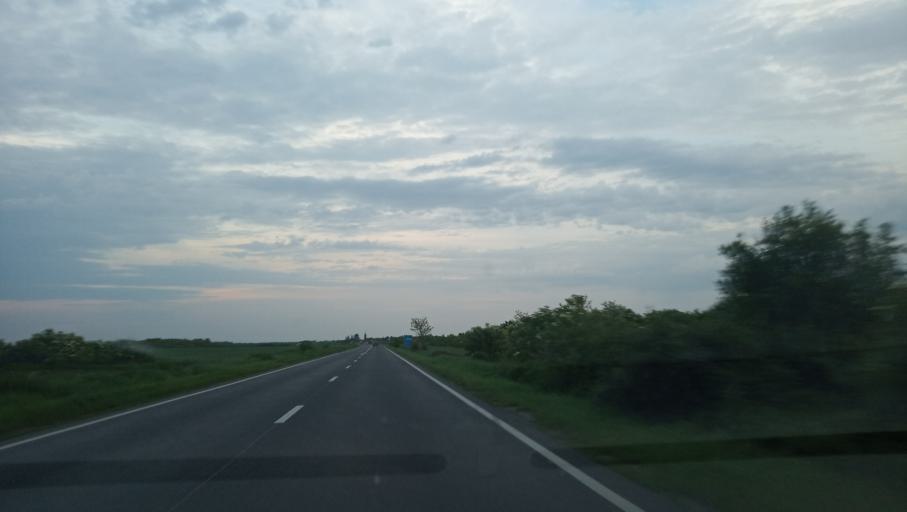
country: RO
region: Timis
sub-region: Comuna Voiteg
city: Voiteg
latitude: 45.4920
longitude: 21.2354
